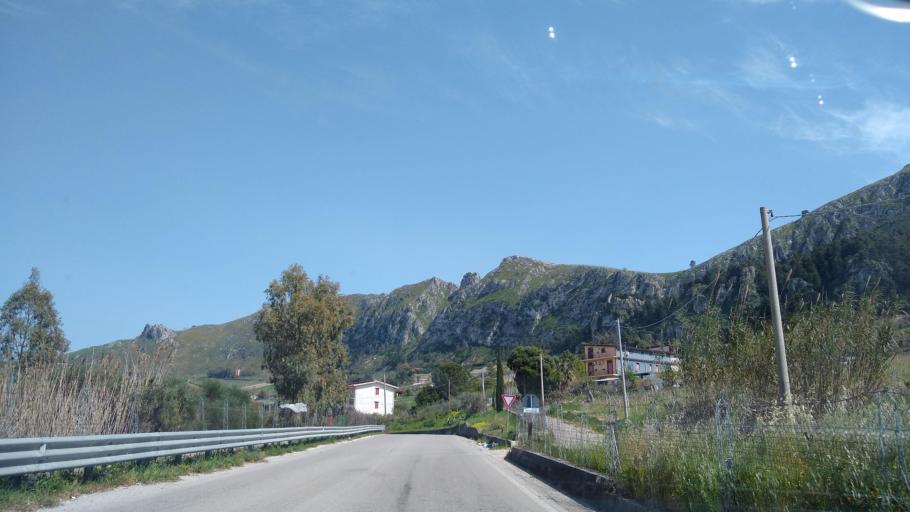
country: IT
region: Sicily
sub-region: Palermo
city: San Giuseppe Jato
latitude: 37.9756
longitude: 13.2014
